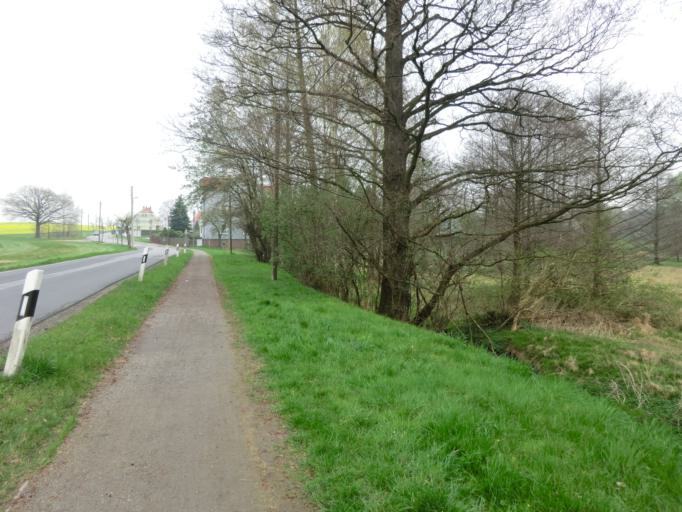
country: DE
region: Saxony
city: Ottendorf-Okrilla
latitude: 51.1294
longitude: 13.8487
